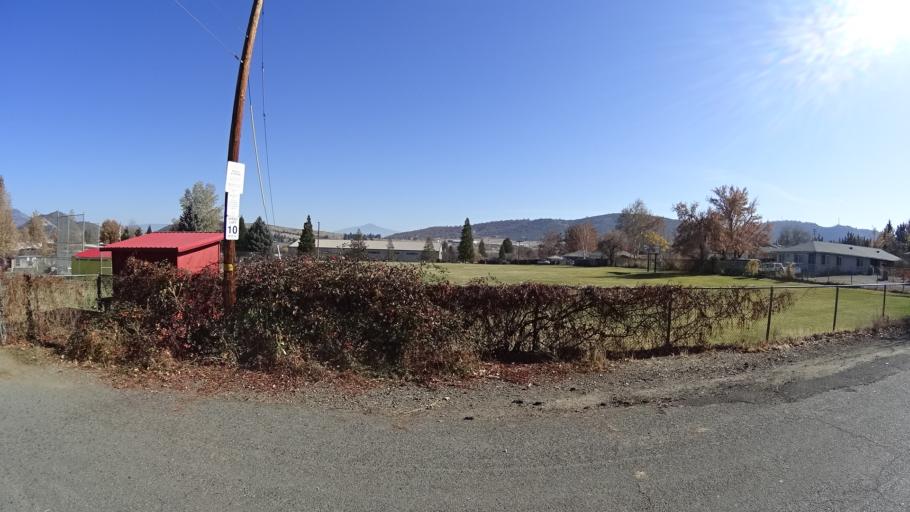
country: US
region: California
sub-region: Siskiyou County
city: Yreka
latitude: 41.7402
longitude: -122.6393
